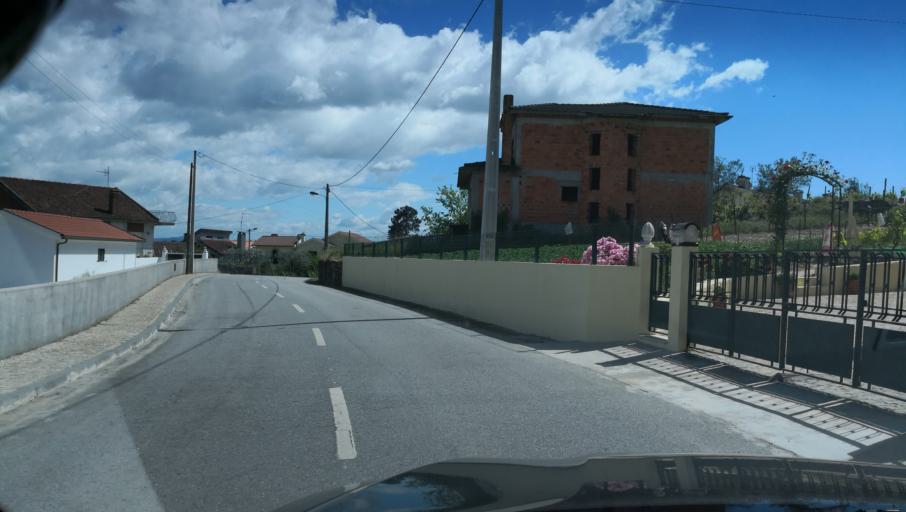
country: PT
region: Vila Real
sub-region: Vila Real
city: Vila Real
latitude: 41.2613
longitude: -7.7323
